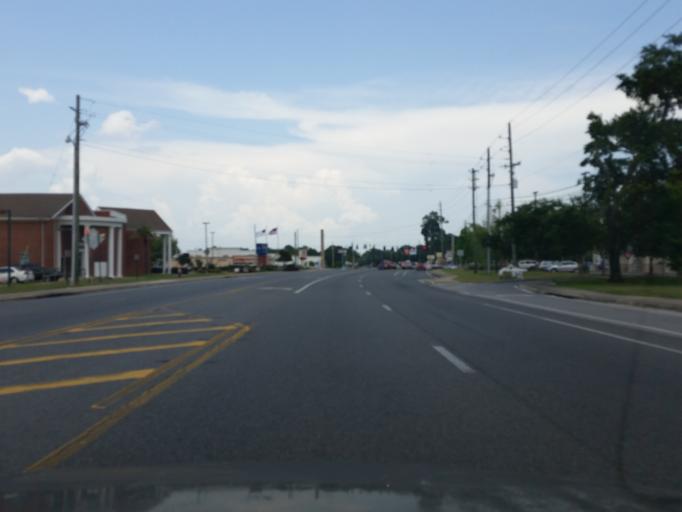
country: US
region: Florida
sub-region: Escambia County
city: Ferry Pass
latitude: 30.5106
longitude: -87.2228
